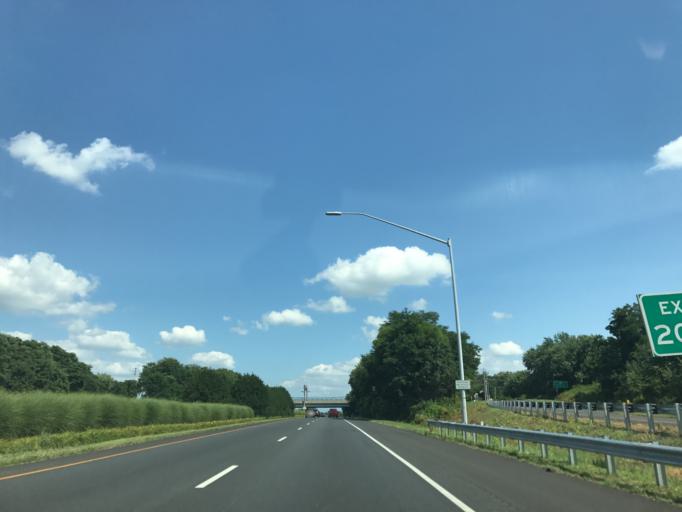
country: US
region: Maryland
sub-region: Howard County
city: Highland
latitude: 39.2092
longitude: -76.9453
